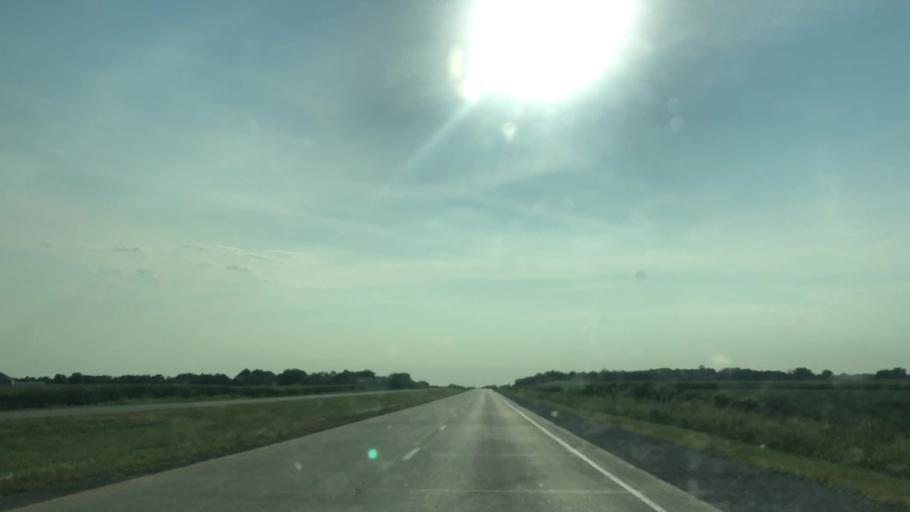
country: US
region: Iowa
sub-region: Story County
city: Nevada
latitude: 42.0082
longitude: -93.3621
